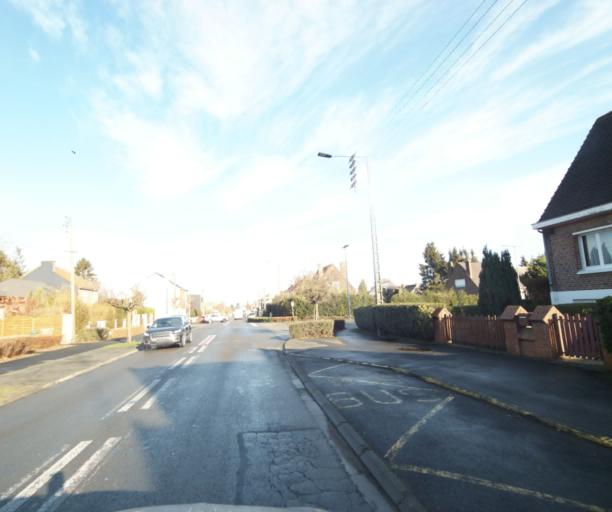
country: FR
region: Nord-Pas-de-Calais
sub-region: Departement du Nord
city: Famars
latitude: 50.3240
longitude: 3.5198
